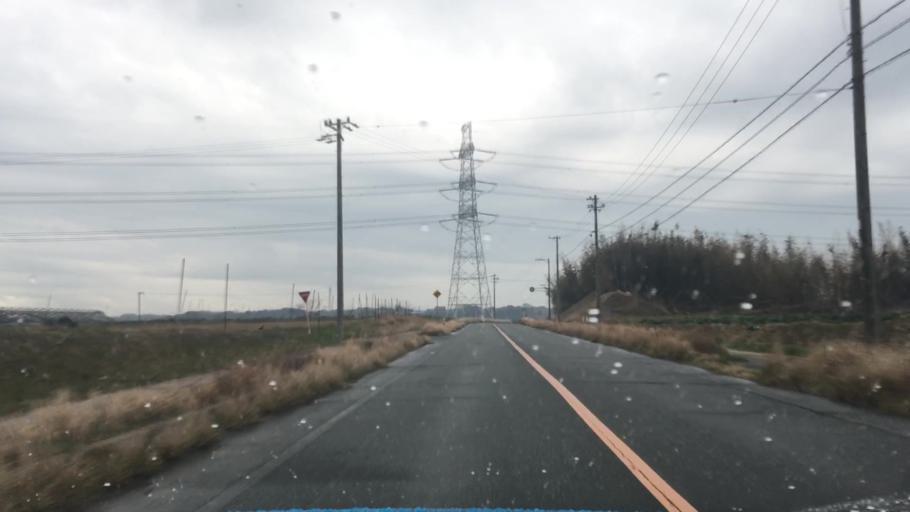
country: JP
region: Aichi
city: Toyohashi
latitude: 34.6765
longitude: 137.3907
